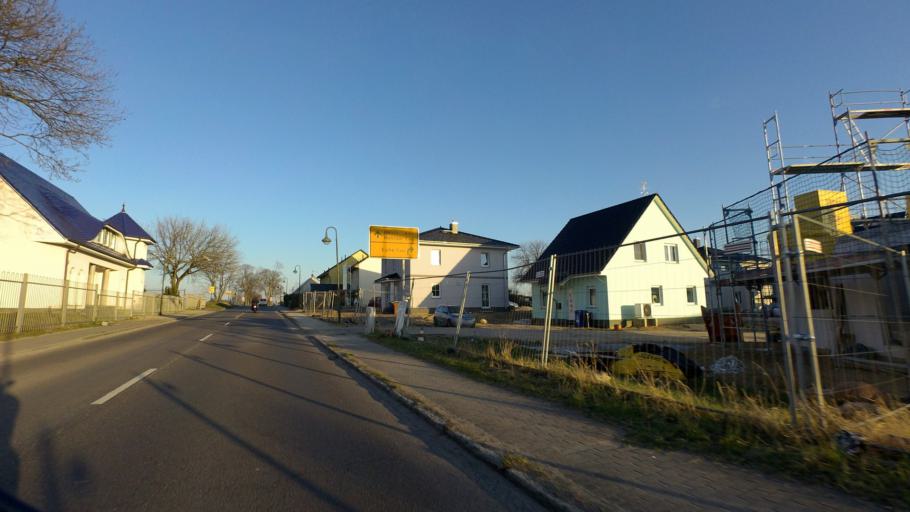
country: DE
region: Brandenburg
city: Ahrensfelde
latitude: 52.5761
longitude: 13.5856
